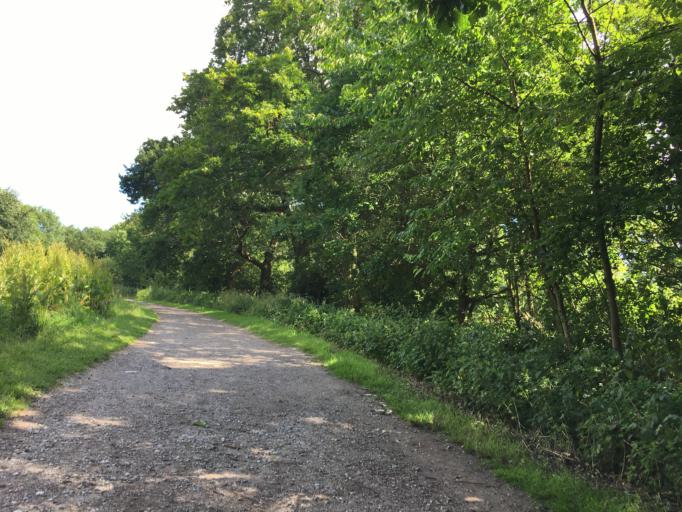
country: GB
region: England
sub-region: Greater London
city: Belsize Park
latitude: 51.5719
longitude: -0.1826
